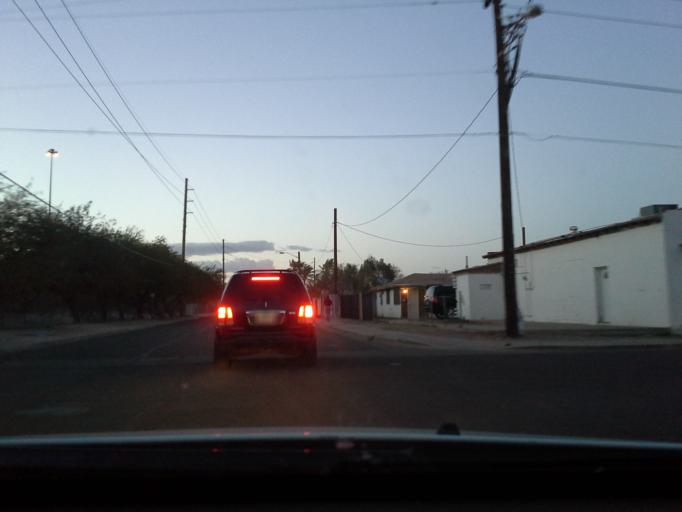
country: US
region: Arizona
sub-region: Maricopa County
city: Phoenix
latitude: 33.4550
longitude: -112.0360
